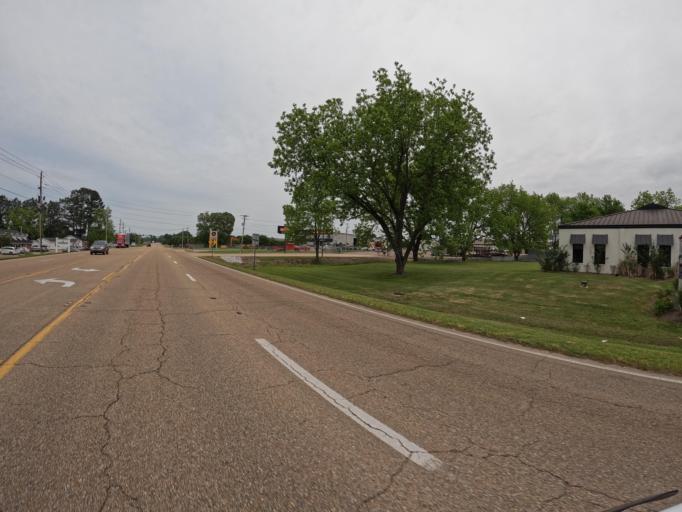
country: US
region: Mississippi
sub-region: Lee County
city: Tupelo
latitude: 34.2945
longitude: -88.7623
